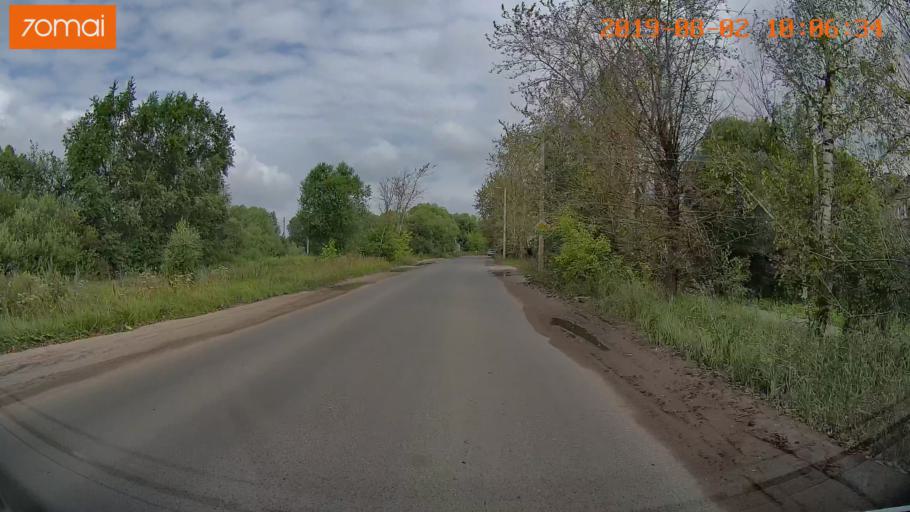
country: RU
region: Ivanovo
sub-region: Gorod Ivanovo
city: Ivanovo
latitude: 56.9792
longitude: 40.9352
